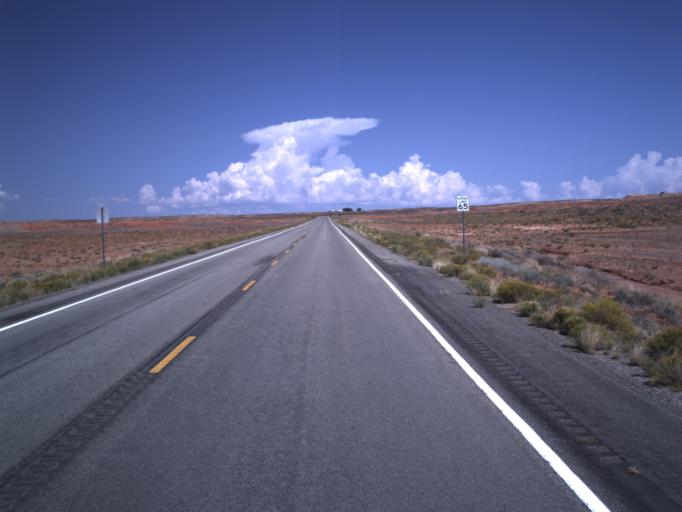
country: US
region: Utah
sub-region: San Juan County
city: Blanding
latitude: 37.0039
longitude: -109.6105
